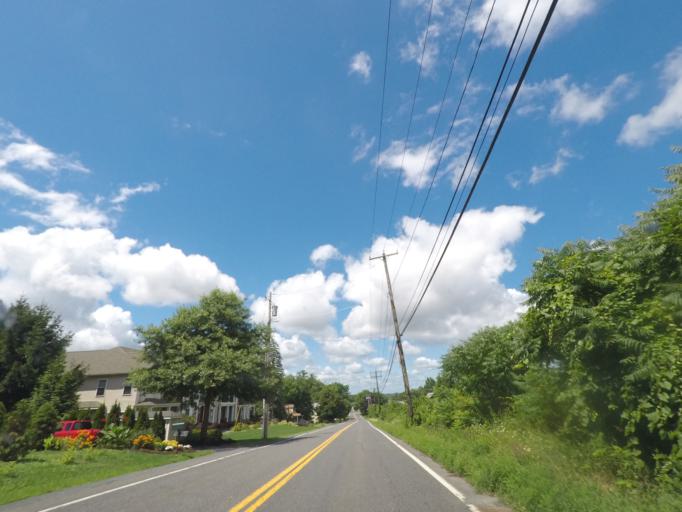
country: US
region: New York
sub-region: Rensselaer County
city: Troy
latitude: 42.6900
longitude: -73.6838
